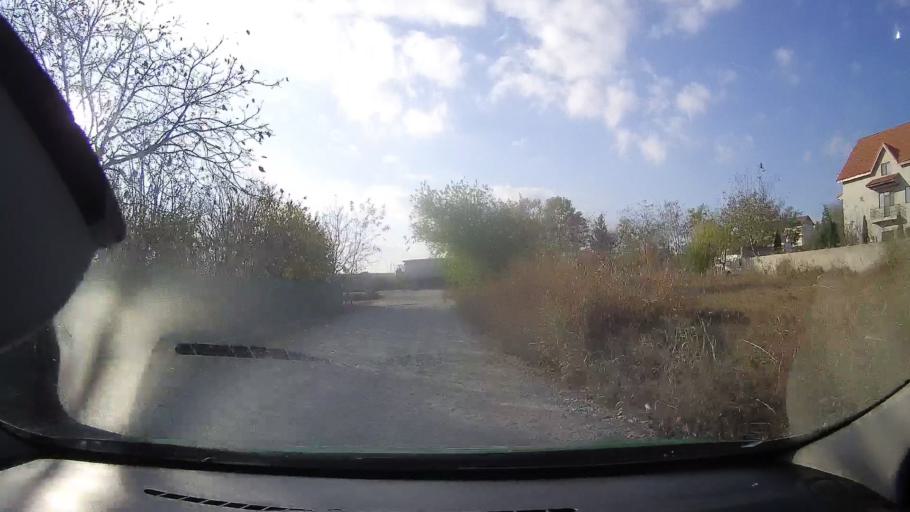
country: RO
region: Constanta
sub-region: Comuna Lumina
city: Lumina
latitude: 44.2875
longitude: 28.5574
